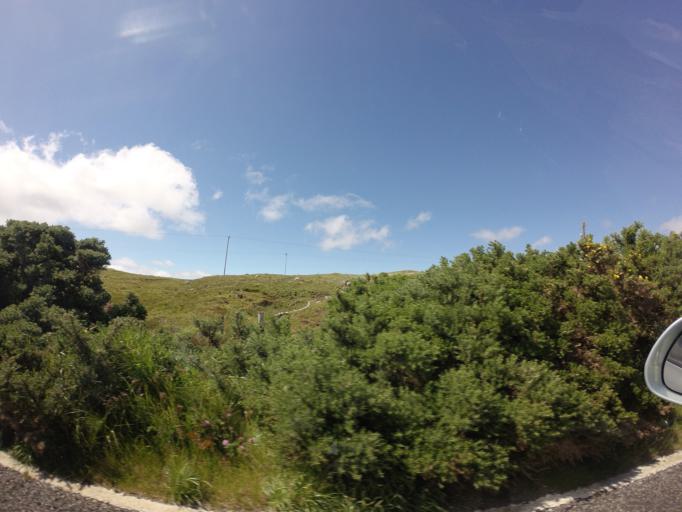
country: GB
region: Scotland
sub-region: Eilean Siar
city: Stornoway
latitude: 58.1152
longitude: -6.5126
